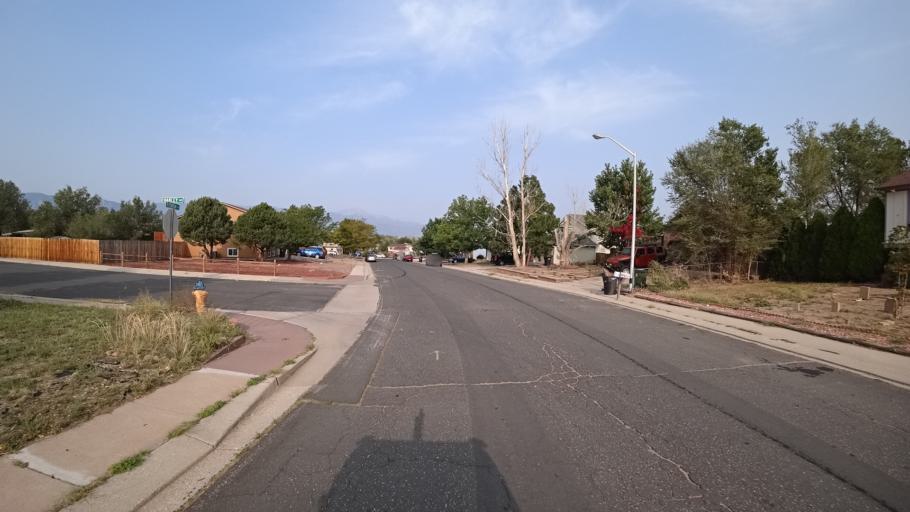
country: US
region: Colorado
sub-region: El Paso County
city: Stratmoor
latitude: 38.8066
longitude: -104.7412
